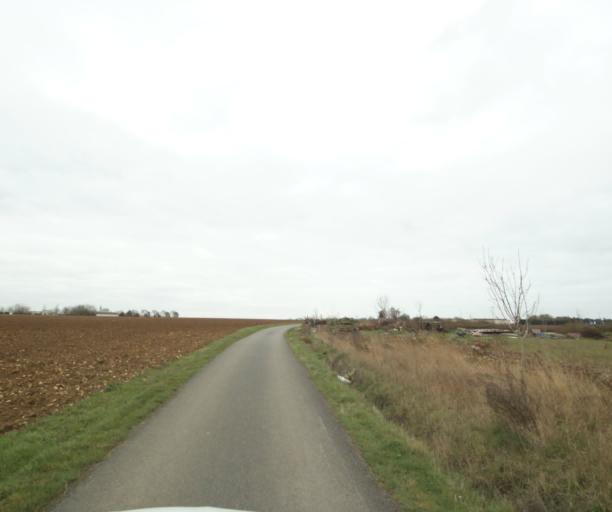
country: FR
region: Poitou-Charentes
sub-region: Departement de la Charente-Maritime
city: Nieul-sur-Mer
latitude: 46.1959
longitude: -1.1662
